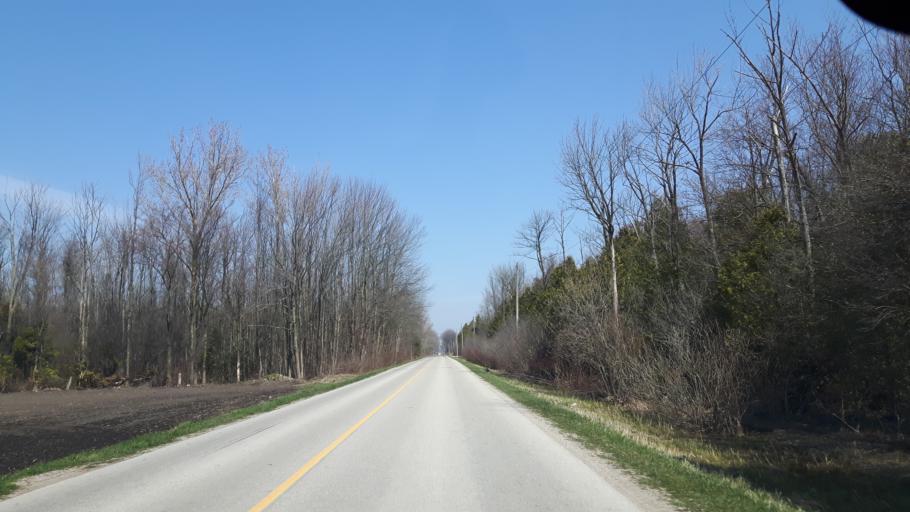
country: CA
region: Ontario
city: Goderich
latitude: 43.6868
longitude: -81.6847
